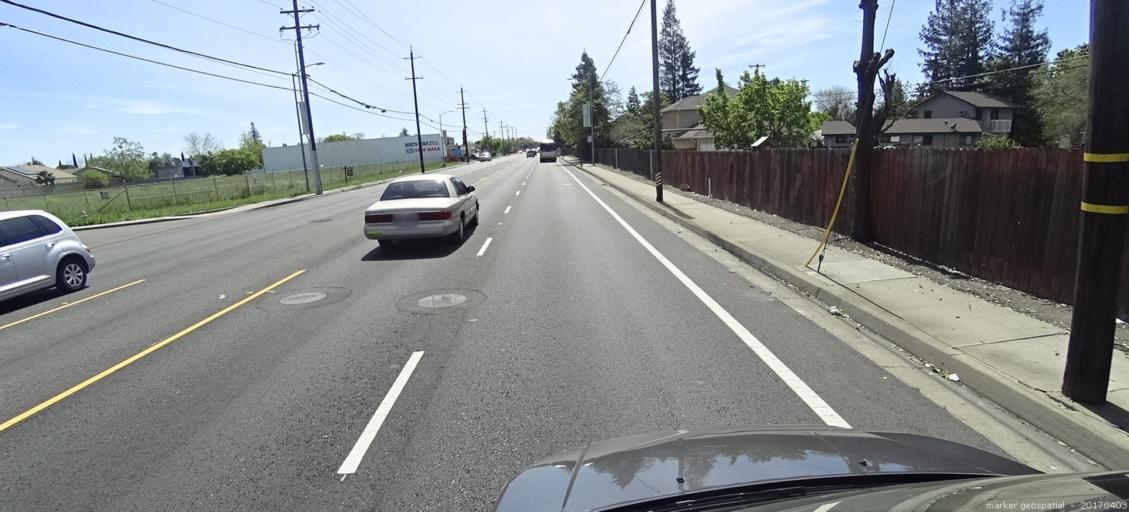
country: US
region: California
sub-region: Sacramento County
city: Sacramento
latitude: 38.6260
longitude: -121.4756
